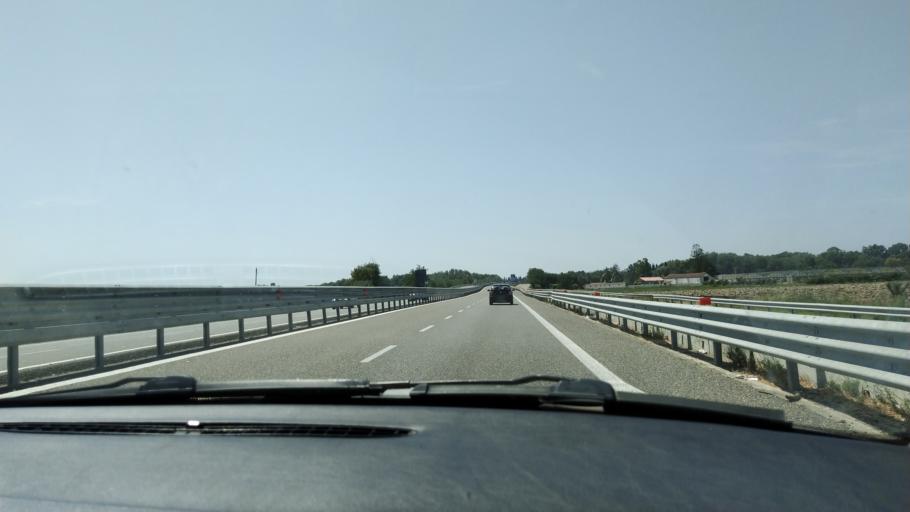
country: IT
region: Basilicate
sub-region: Provincia di Matera
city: Marconia
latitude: 40.3709
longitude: 16.7846
